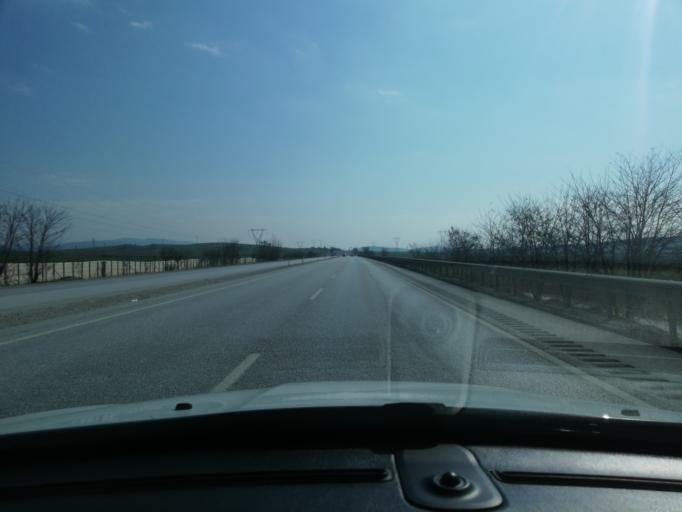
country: TR
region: Cankiri
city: Kursunlu
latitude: 40.8422
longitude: 33.1720
